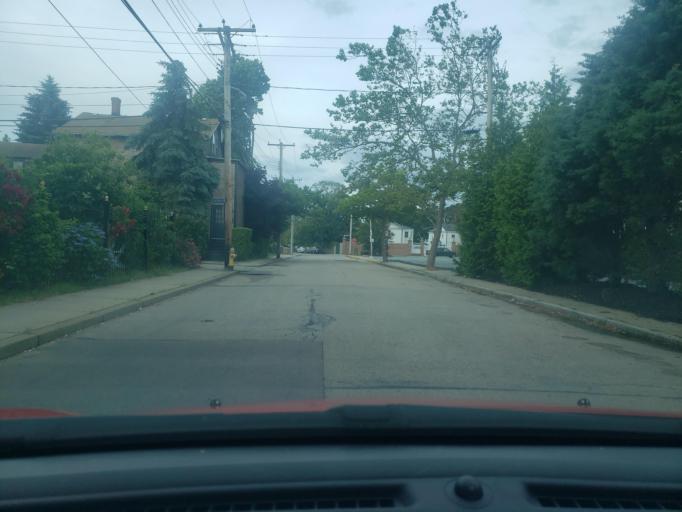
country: US
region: Rhode Island
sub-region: Newport County
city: Newport
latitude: 41.4815
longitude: -71.3062
